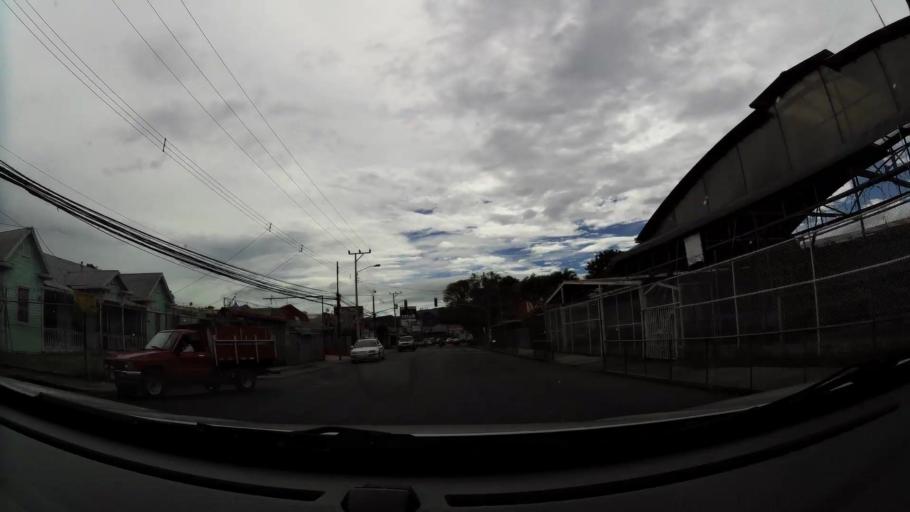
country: CR
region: San Jose
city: San Pedro
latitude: 9.9225
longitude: -84.0549
